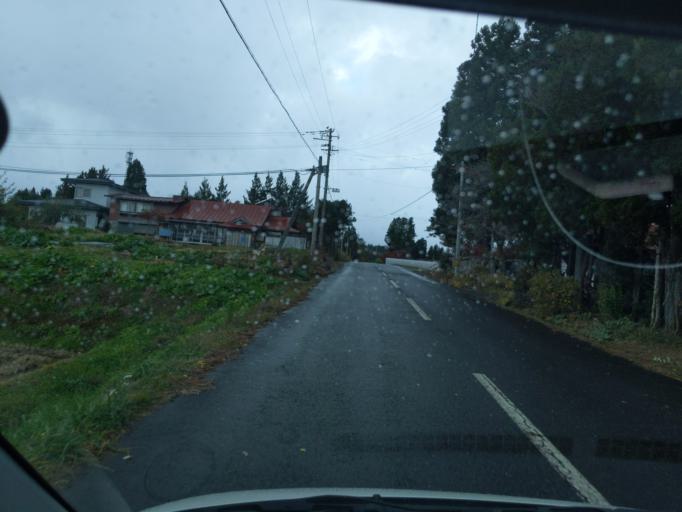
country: JP
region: Iwate
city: Mizusawa
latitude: 39.0945
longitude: 140.9888
